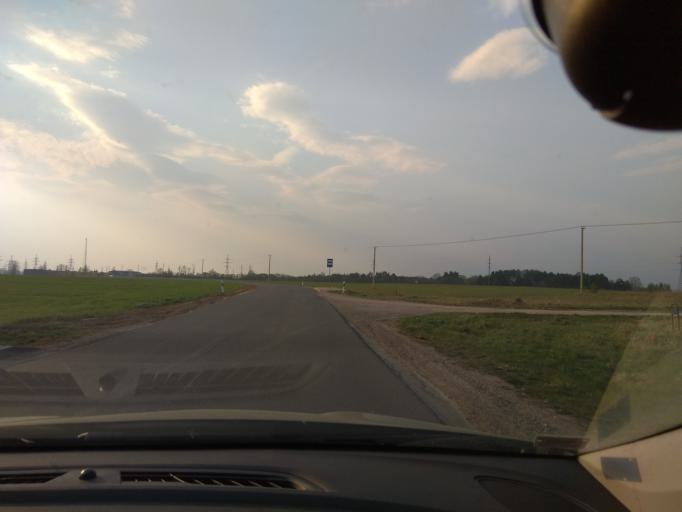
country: LT
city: Baltoji Voke
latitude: 54.6083
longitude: 25.1295
